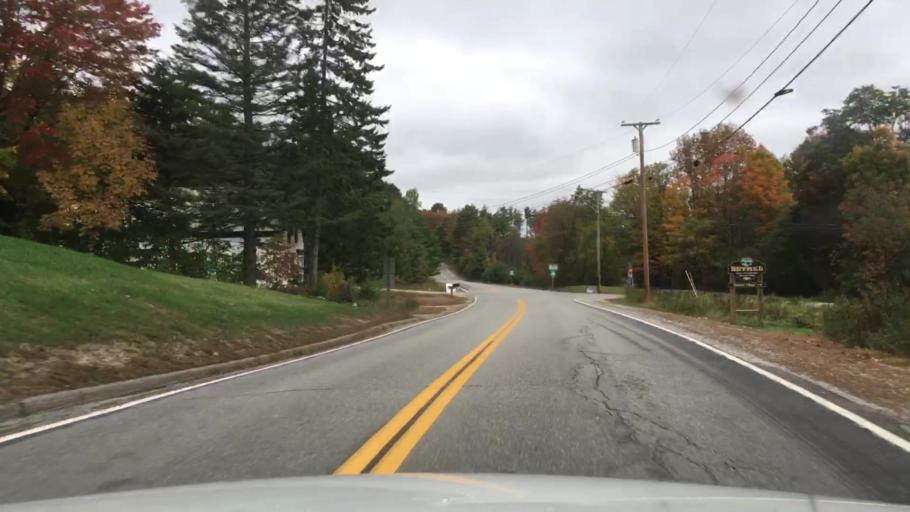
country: US
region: Maine
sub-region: Oxford County
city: Bethel
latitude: 44.4015
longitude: -70.7949
